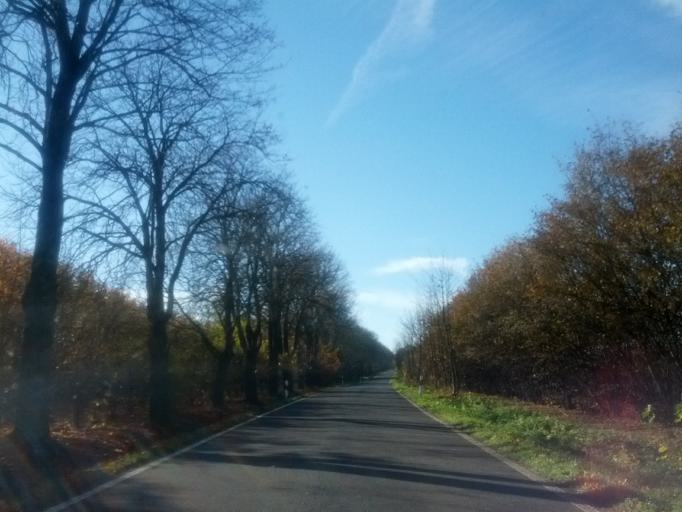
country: DE
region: Thuringia
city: Friedrichswerth
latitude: 50.9673
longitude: 10.5668
